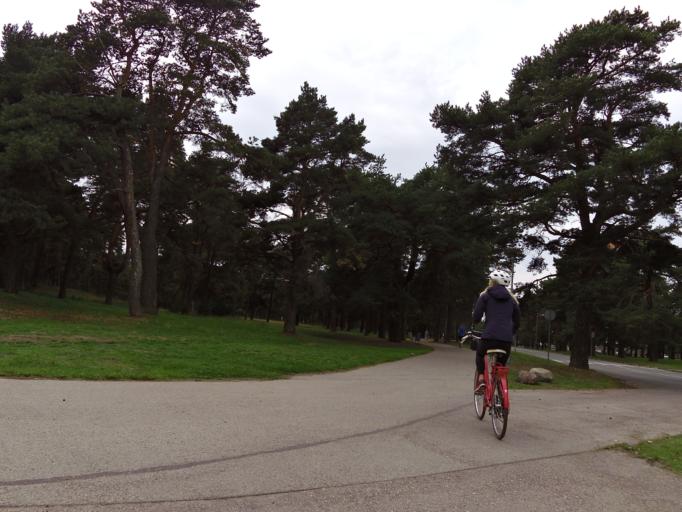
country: EE
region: Harju
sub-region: Tallinna linn
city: Tallinn
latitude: 59.4412
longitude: 24.6918
